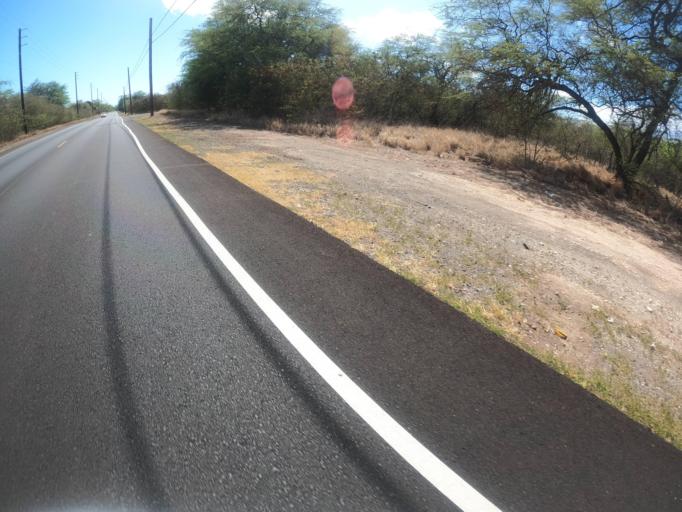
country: US
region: Hawaii
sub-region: Honolulu County
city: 'Ewa Villages
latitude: 21.3123
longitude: -158.0557
